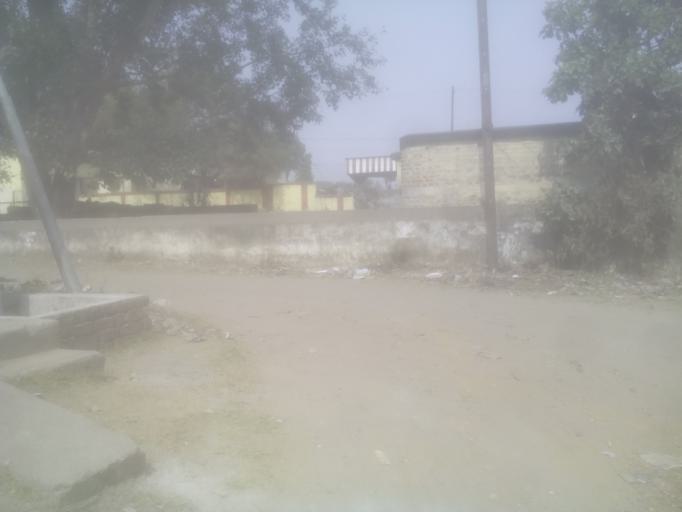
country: IN
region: Jharkhand
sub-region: Bokaro
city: Dugda
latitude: 23.7547
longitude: 86.1202
